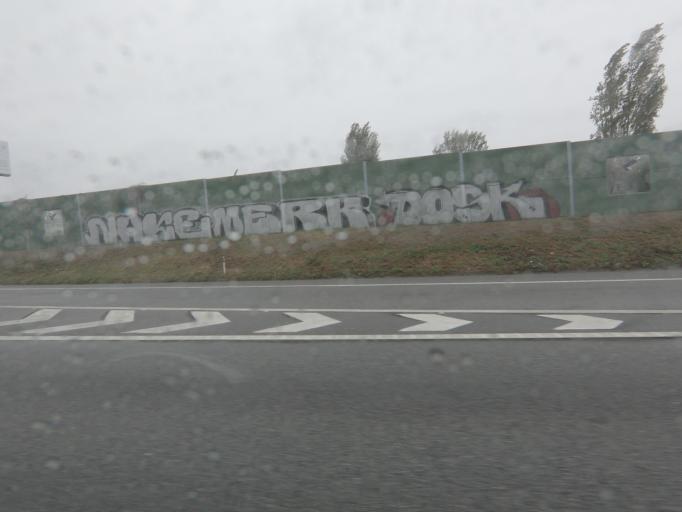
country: PT
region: Porto
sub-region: Maia
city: Pedroucos
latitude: 41.1838
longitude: -8.5937
